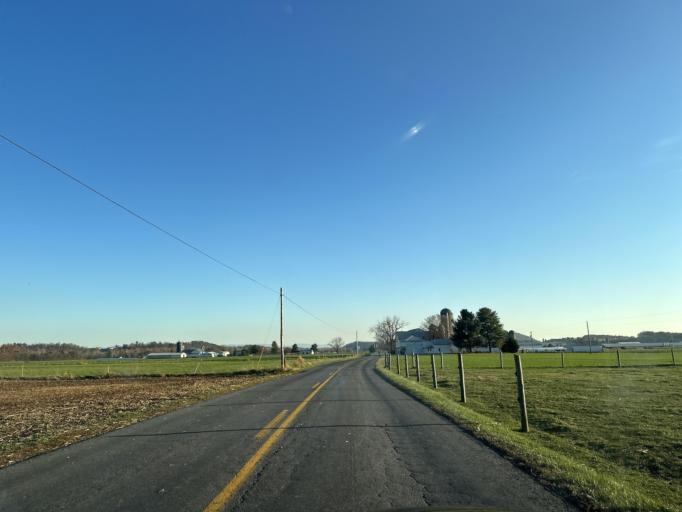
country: US
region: Virginia
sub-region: Rockingham County
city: Bridgewater
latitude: 38.4409
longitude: -78.9961
